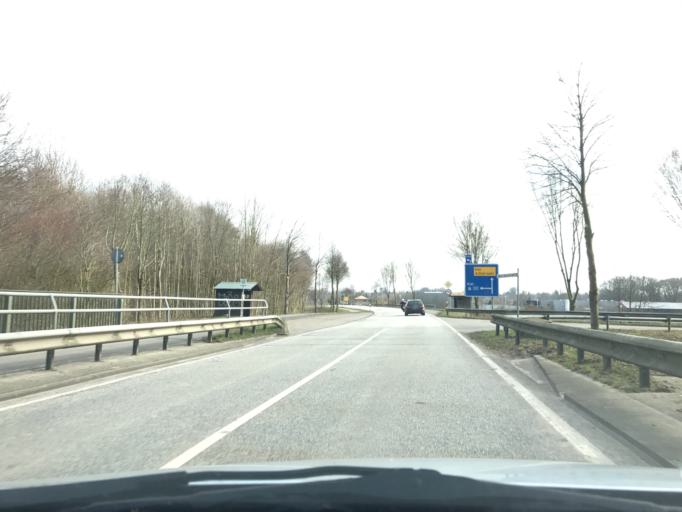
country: DE
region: Schleswig-Holstein
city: Achterwehr
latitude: 54.3193
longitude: 9.9493
